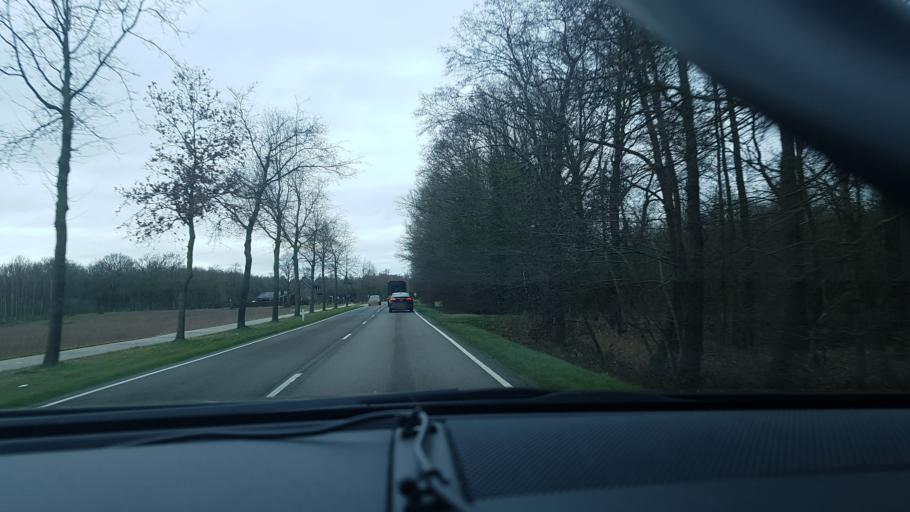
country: NL
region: Limburg
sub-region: Gemeente Leudal
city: Heythuysen
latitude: 51.3062
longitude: 5.8905
